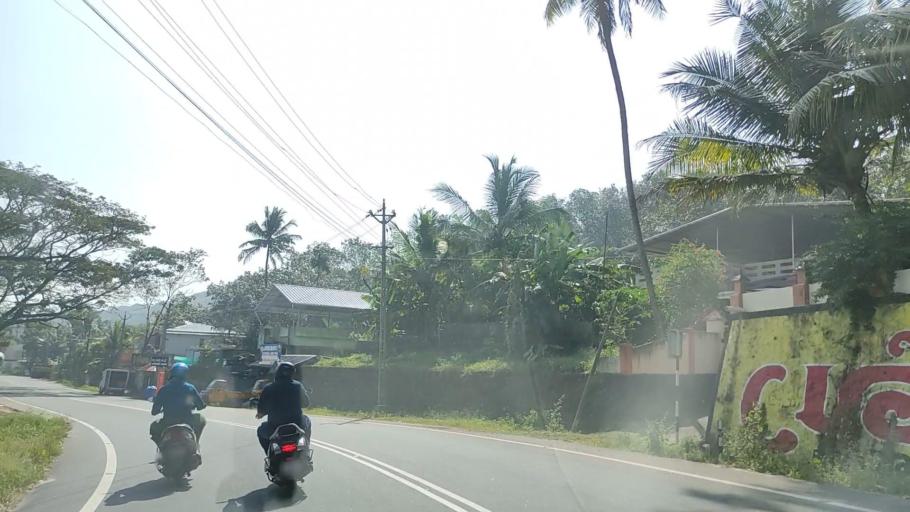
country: IN
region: Kerala
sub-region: Kollam
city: Punalur
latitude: 8.9351
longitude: 76.9534
